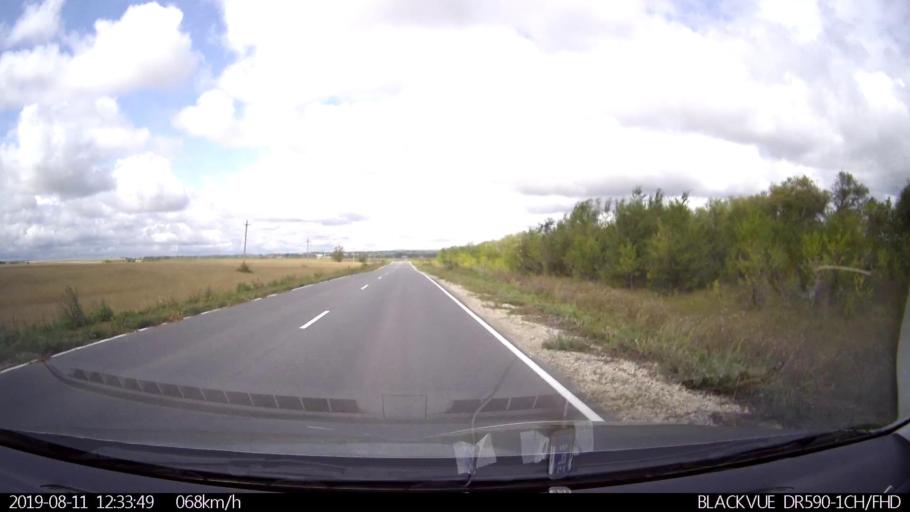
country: RU
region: Ulyanovsk
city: Ignatovka
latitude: 53.8123
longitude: 47.8510
